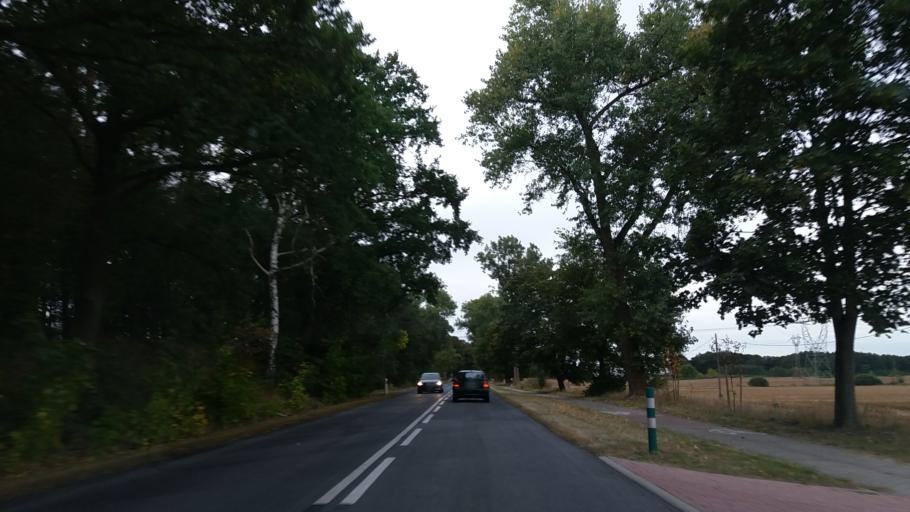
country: PL
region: Lubusz
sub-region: Powiat gorzowski
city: Klodawa
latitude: 52.7984
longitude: 15.2182
